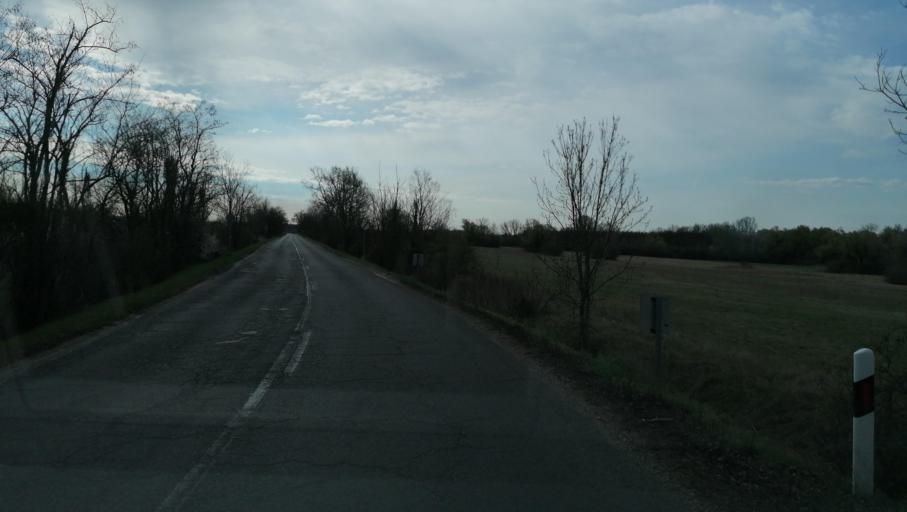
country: HU
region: Pest
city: Ocsa
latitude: 47.2788
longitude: 19.2363
